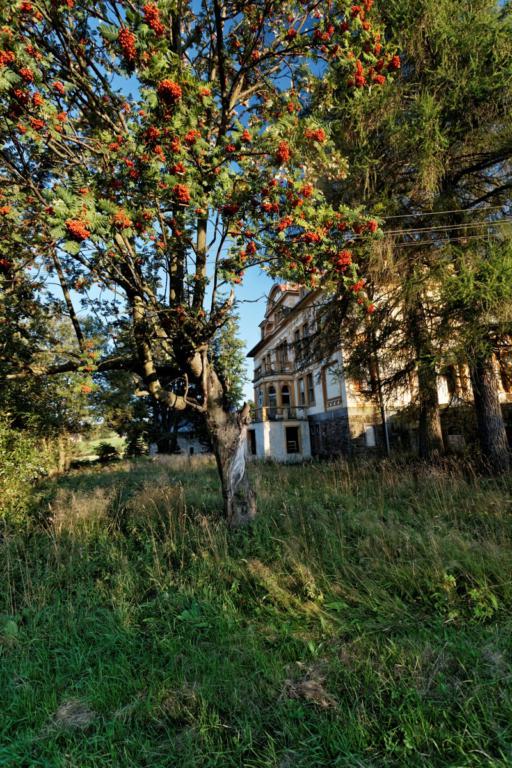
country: CZ
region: Ustecky
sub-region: Okres Chomutov
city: Kovarska
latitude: 50.4328
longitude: 13.0450
